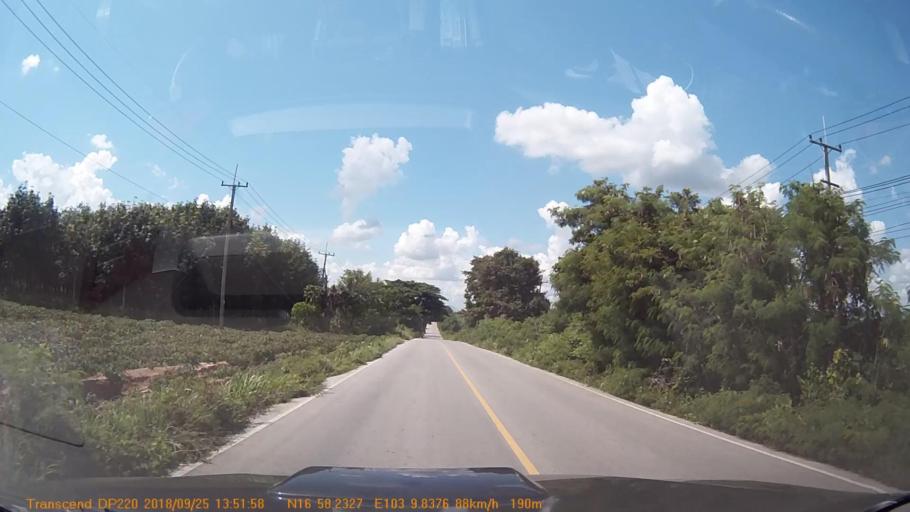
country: TH
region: Changwat Udon Thani
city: Si That
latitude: 16.9707
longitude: 103.1639
